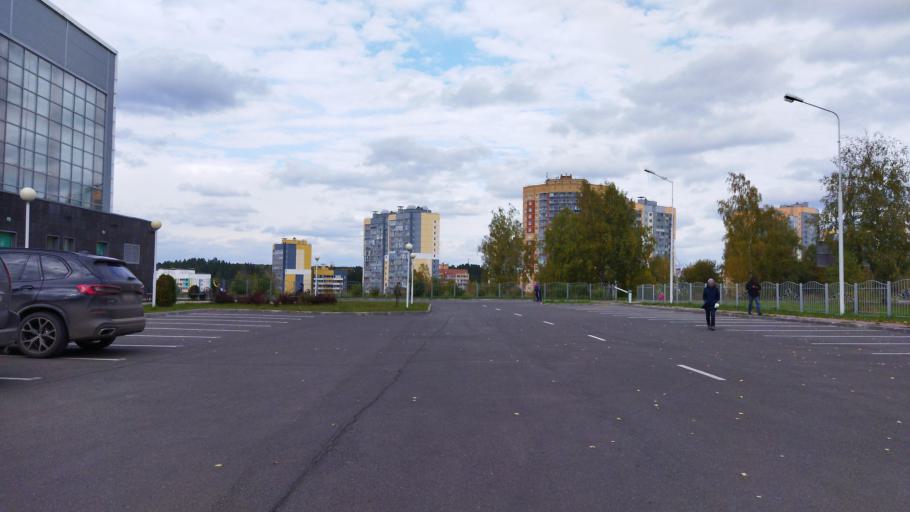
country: RU
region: Tomsk
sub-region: Tomskiy Rayon
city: Tomsk
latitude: 56.4938
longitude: 85.0594
